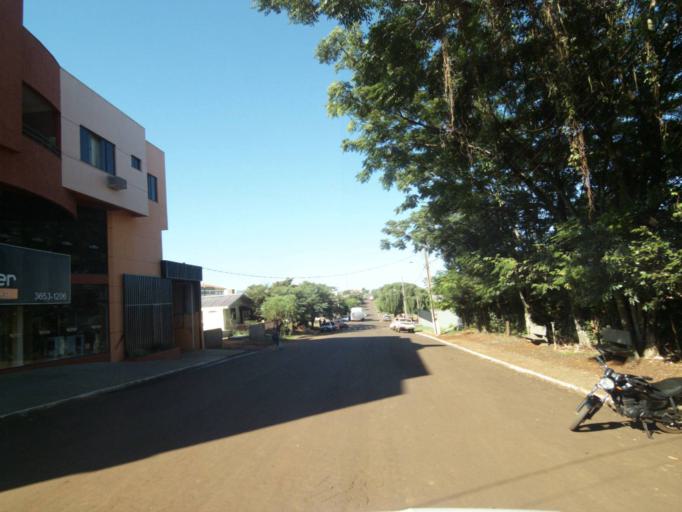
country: BR
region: Parana
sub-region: Laranjeiras Do Sul
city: Laranjeiras do Sul
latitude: -25.4894
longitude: -52.5267
